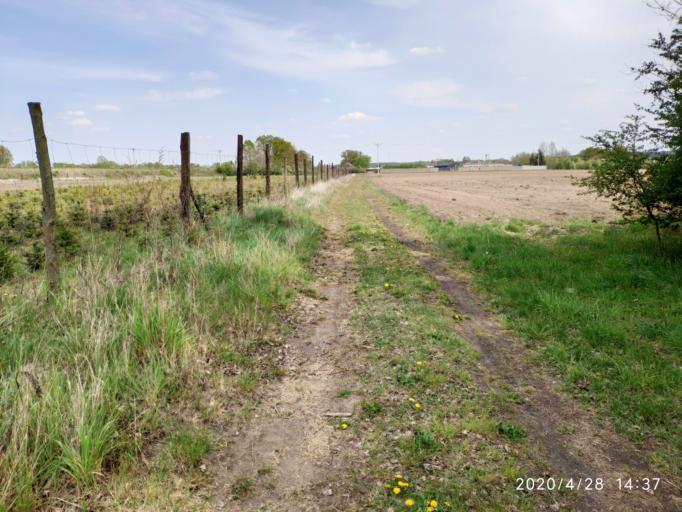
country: PL
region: Lubusz
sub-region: Powiat krosnienski
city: Krosno Odrzanskie
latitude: 52.0331
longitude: 15.0796
